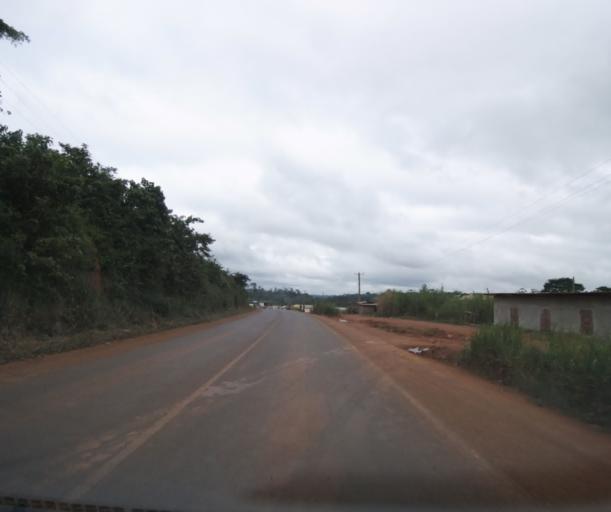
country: CM
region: Centre
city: Yaounde
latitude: 3.7944
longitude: 11.4762
